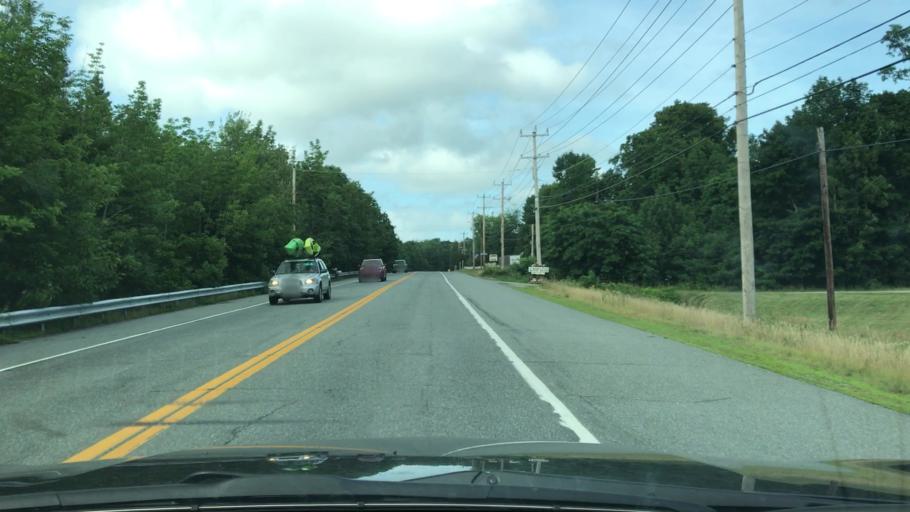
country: US
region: Maine
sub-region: Hancock County
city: Trenton
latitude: 44.4292
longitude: -68.3232
